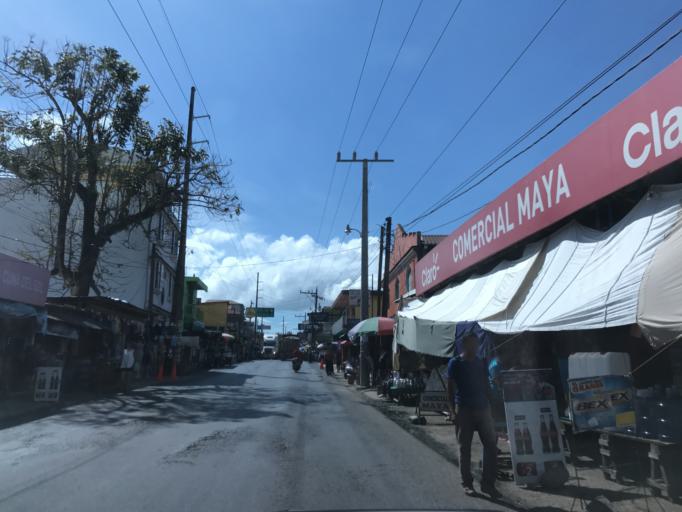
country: GT
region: Izabal
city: Morales
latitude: 15.6599
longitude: -89.0048
